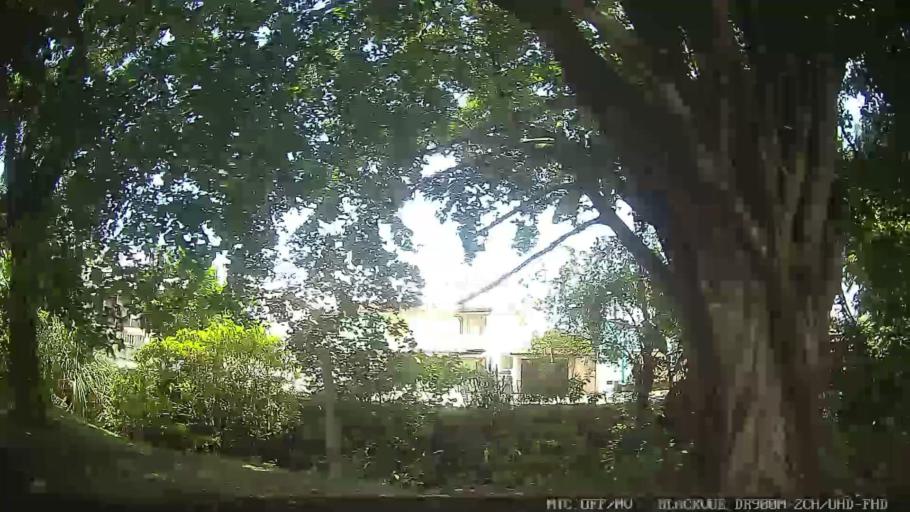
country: BR
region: Sao Paulo
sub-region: Caraguatatuba
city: Caraguatatuba
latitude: -23.6174
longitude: -45.3840
